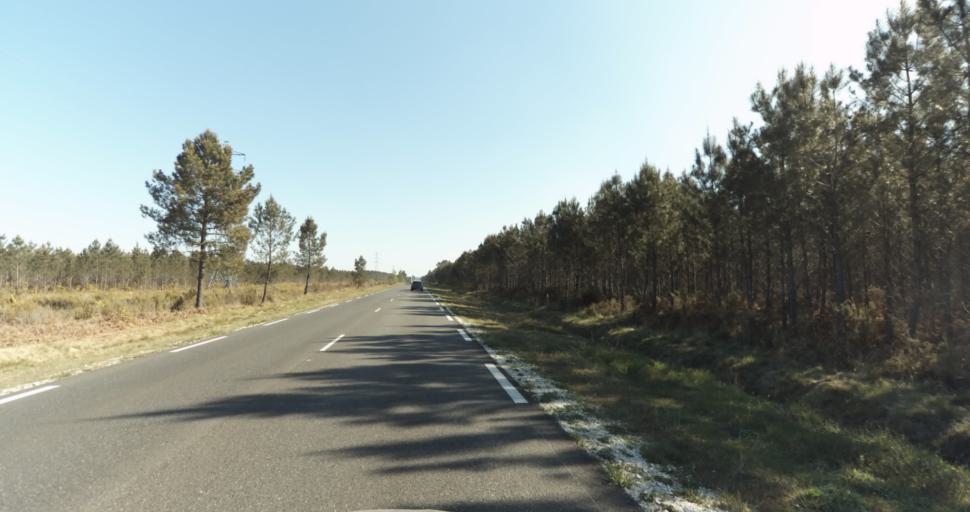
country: FR
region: Aquitaine
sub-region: Departement de la Gironde
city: Martignas-sur-Jalle
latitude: 44.8029
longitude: -0.8662
